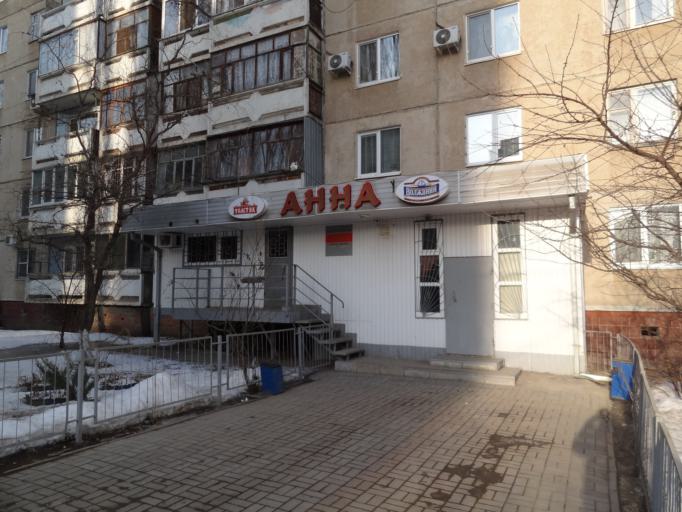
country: RU
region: Saratov
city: Engel's
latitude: 51.4770
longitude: 46.1381
